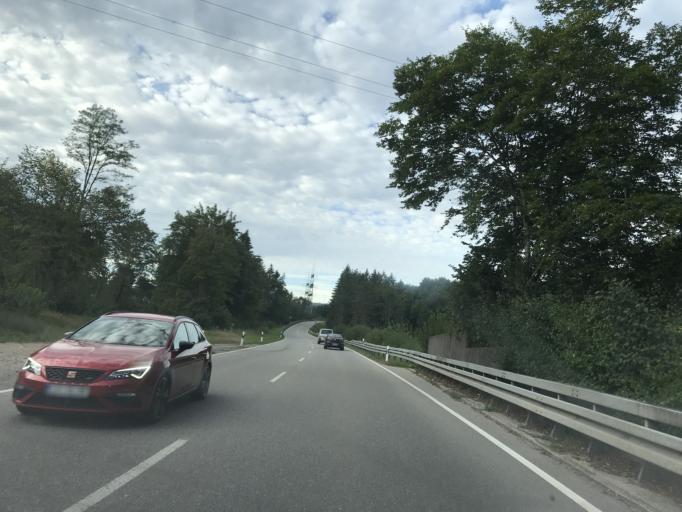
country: DE
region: Baden-Wuerttemberg
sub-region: Freiburg Region
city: Wehr
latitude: 47.5999
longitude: 7.9133
